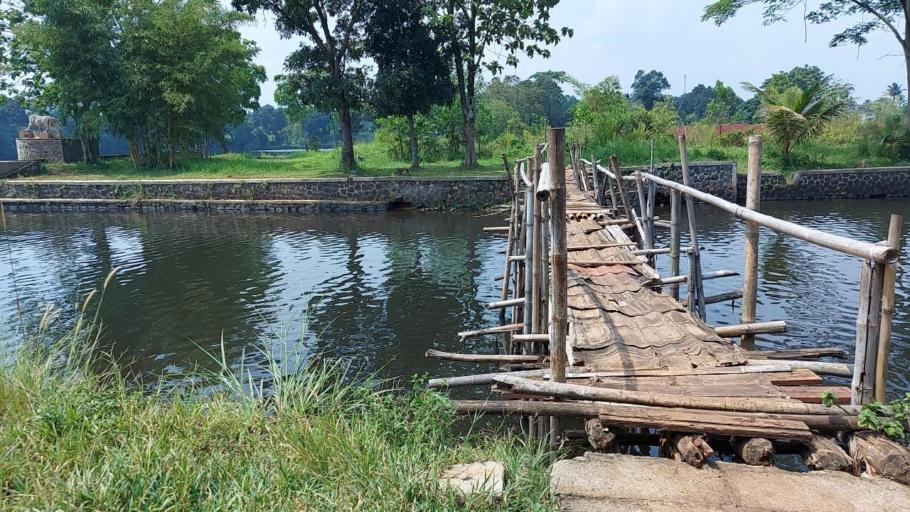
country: ID
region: West Java
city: Cibinong
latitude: -6.5056
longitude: 106.7808
